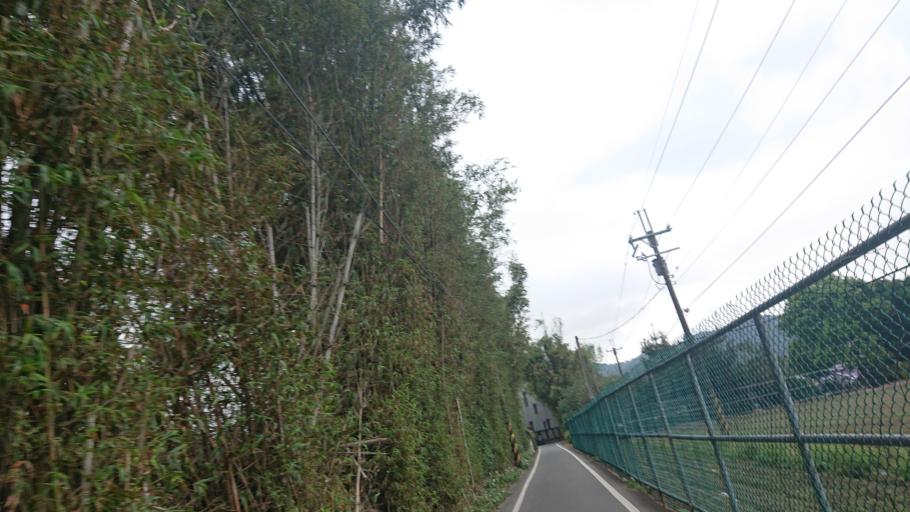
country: TW
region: Taiwan
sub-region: Taoyuan
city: Taoyuan
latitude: 24.9481
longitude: 121.3651
